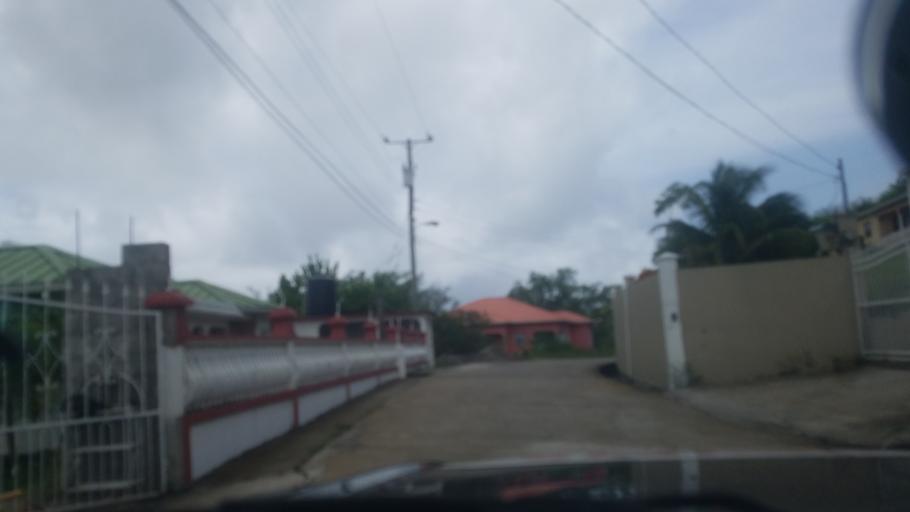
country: LC
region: Laborie Quarter
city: Laborie
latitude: 13.7455
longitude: -60.9649
